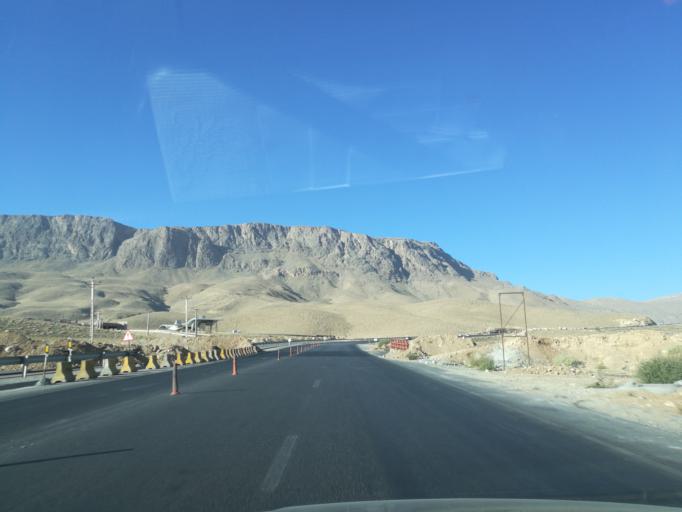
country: IR
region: Chahar Mahall va Bakhtiari
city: Farrokh Shahr
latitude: 32.3461
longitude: 51.1110
